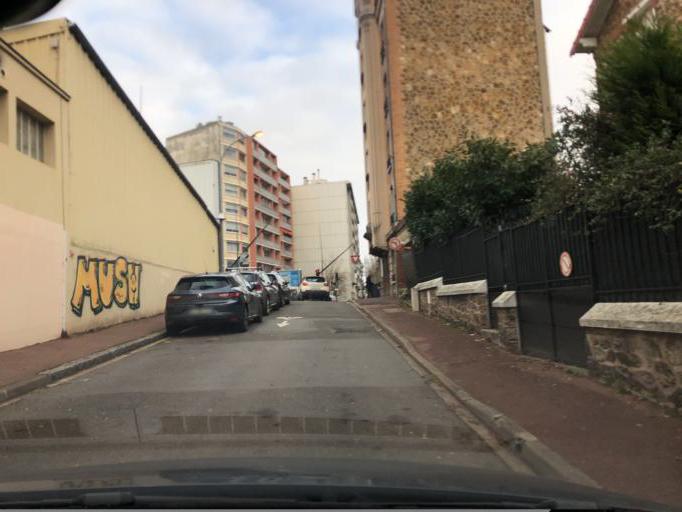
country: FR
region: Ile-de-France
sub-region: Departement des Hauts-de-Seine
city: Chaville
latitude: 48.8049
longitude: 2.1833
